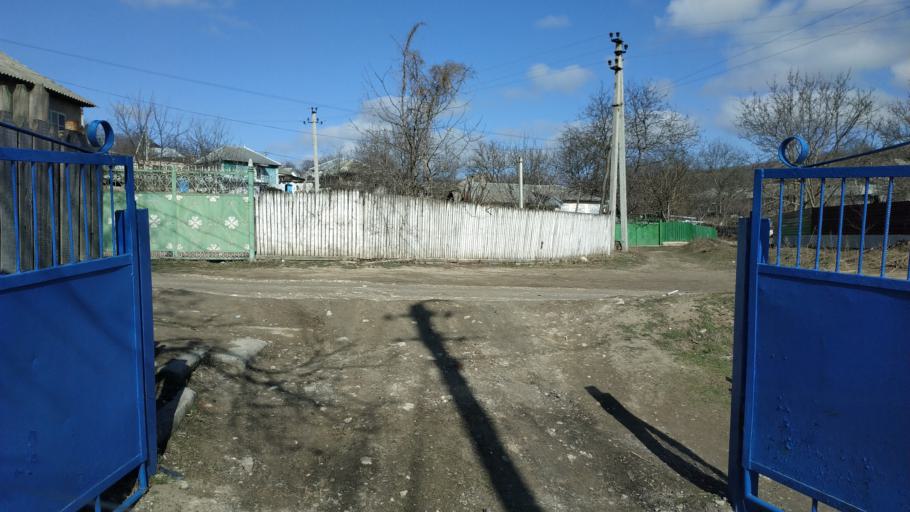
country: MD
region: Straseni
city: Straseni
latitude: 47.0214
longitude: 28.5438
